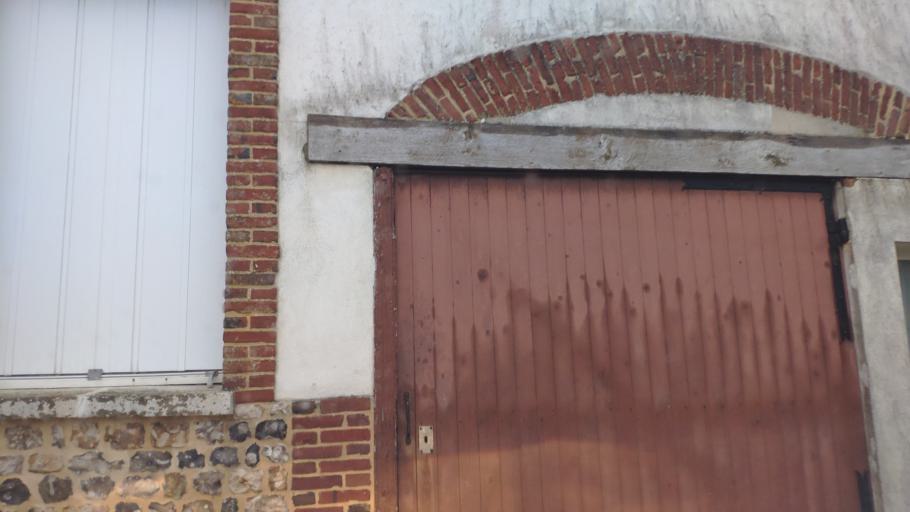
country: FR
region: Haute-Normandie
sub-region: Departement de la Seine-Maritime
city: Doudeville
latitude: 49.7224
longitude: 0.7852
